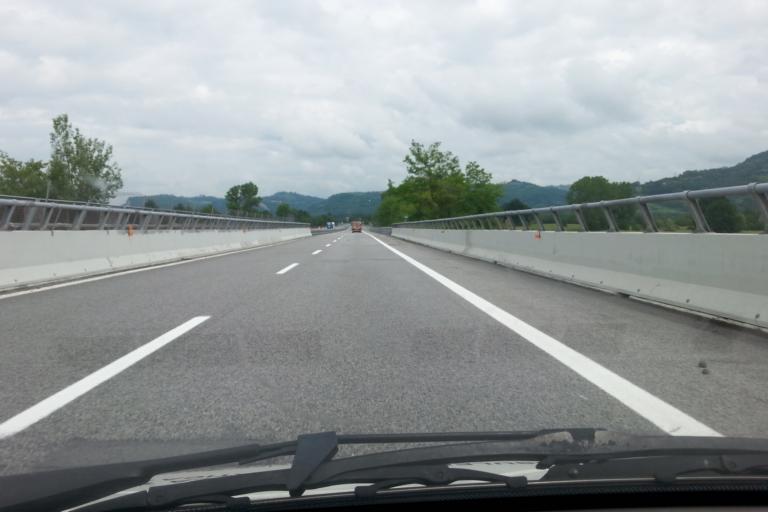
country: IT
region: Piedmont
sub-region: Provincia di Cuneo
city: Lesegno
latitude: 44.4022
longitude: 7.9736
